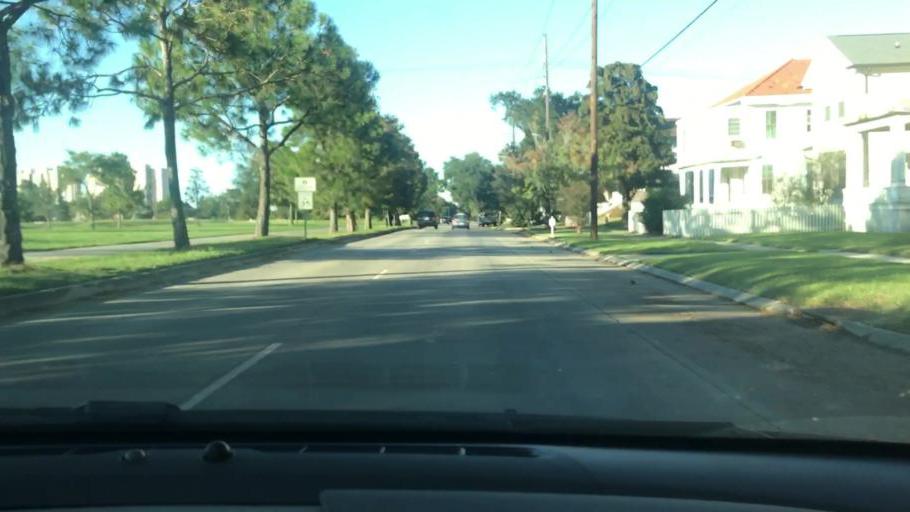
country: US
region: Louisiana
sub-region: Jefferson Parish
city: Metairie
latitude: 30.0136
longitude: -90.1140
